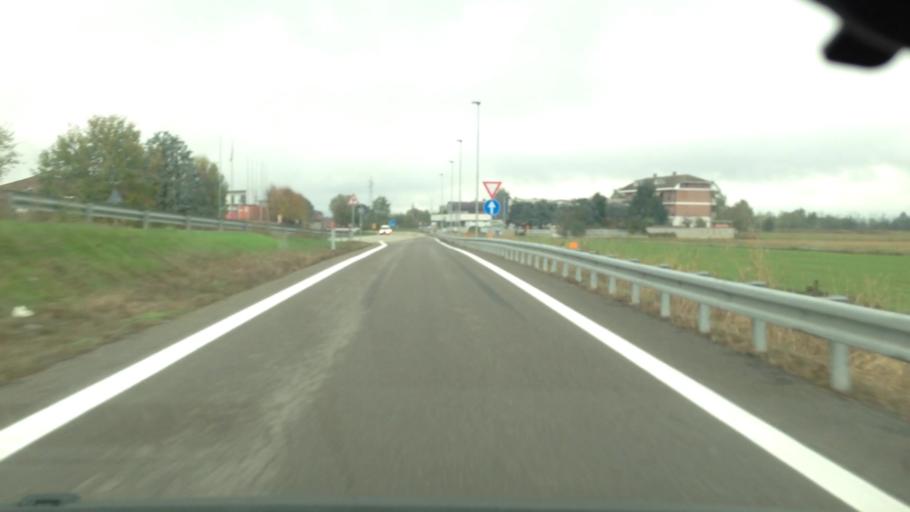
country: IT
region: Piedmont
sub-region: Provincia di Asti
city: Villanova d'Asti
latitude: 44.9559
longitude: 7.9151
